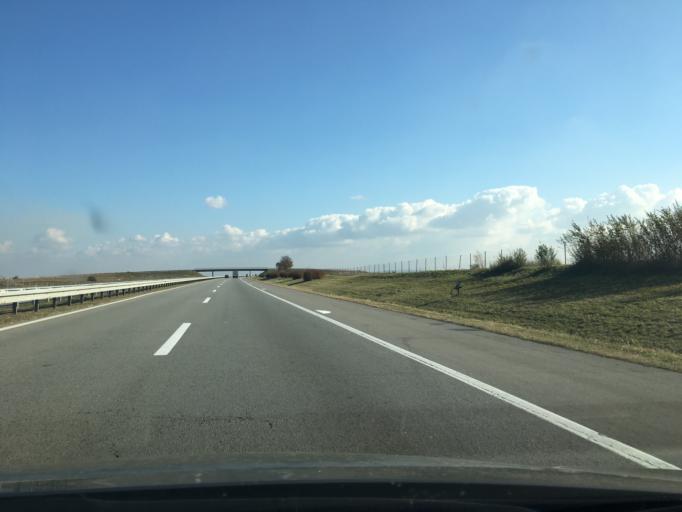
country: RS
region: Autonomna Pokrajina Vojvodina
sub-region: Juznobacki Okrug
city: Kovilj
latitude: 45.2601
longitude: 19.9920
